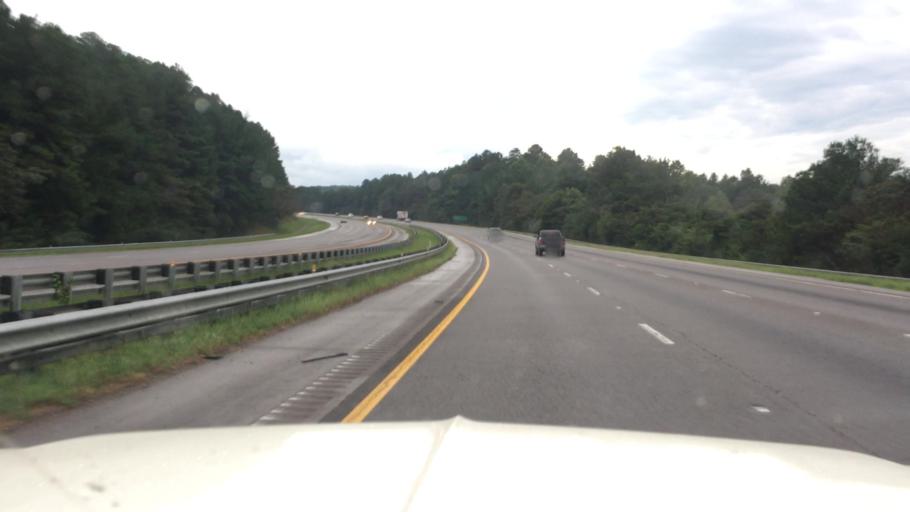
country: US
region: Alabama
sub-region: Jefferson County
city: Mount Olive
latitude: 33.7053
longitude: -86.8366
